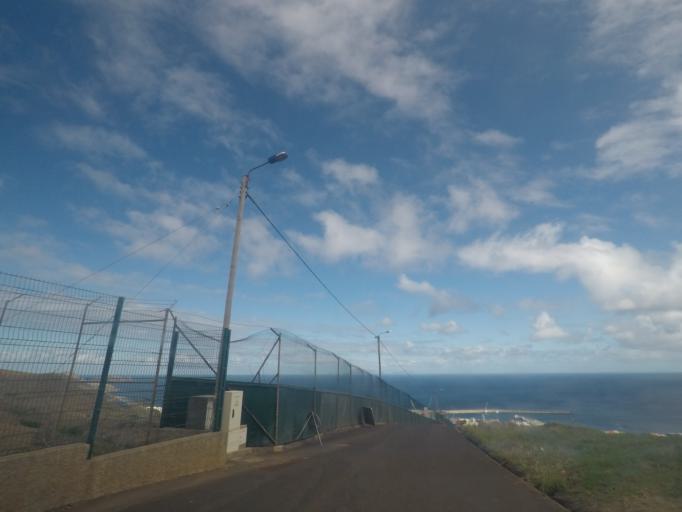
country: PT
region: Madeira
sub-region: Machico
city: Canical
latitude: 32.7465
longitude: -16.7390
